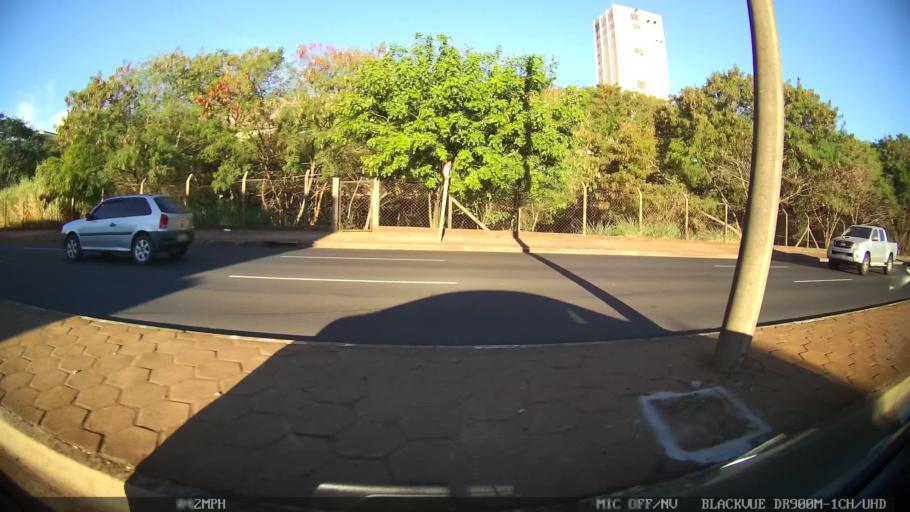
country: BR
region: Sao Paulo
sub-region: Araraquara
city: Araraquara
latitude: -21.7755
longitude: -48.1676
